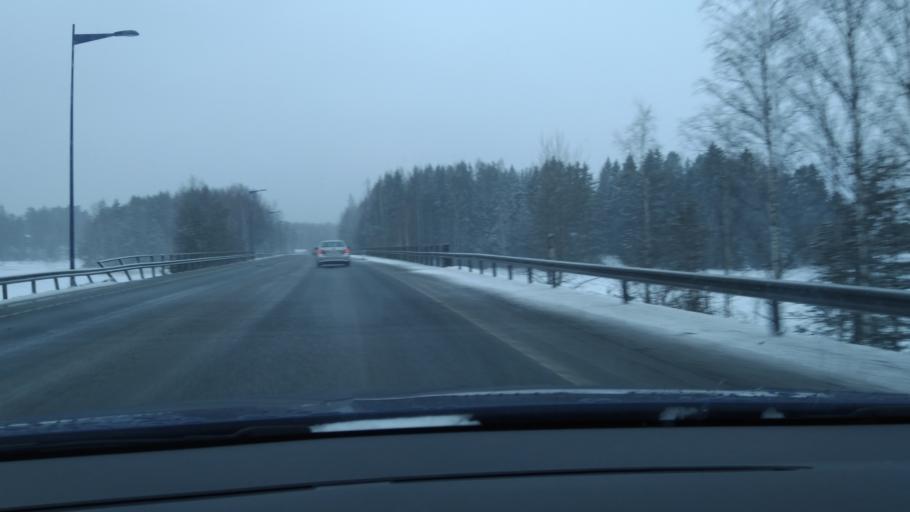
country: FI
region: Pirkanmaa
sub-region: Tampere
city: Tampere
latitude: 61.5246
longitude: 23.9301
